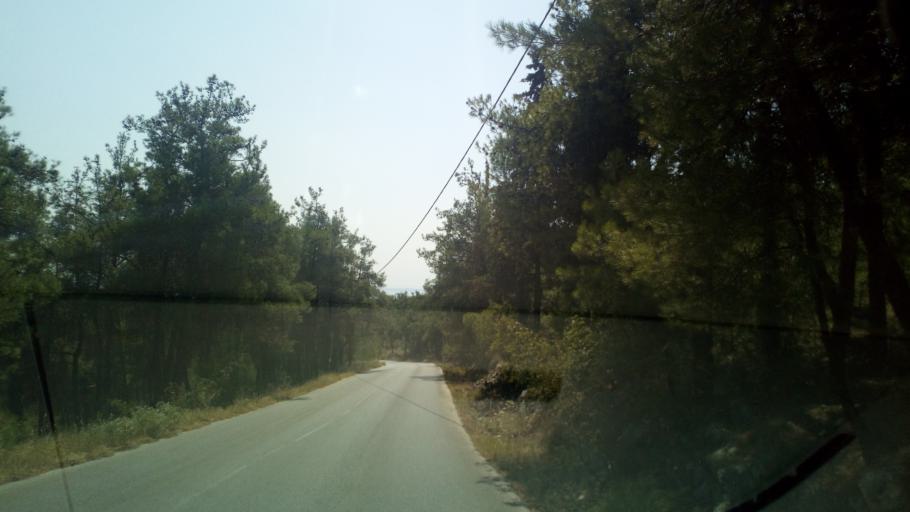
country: GR
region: Central Macedonia
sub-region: Nomos Thessalonikis
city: Pefka
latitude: 40.6444
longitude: 22.9831
